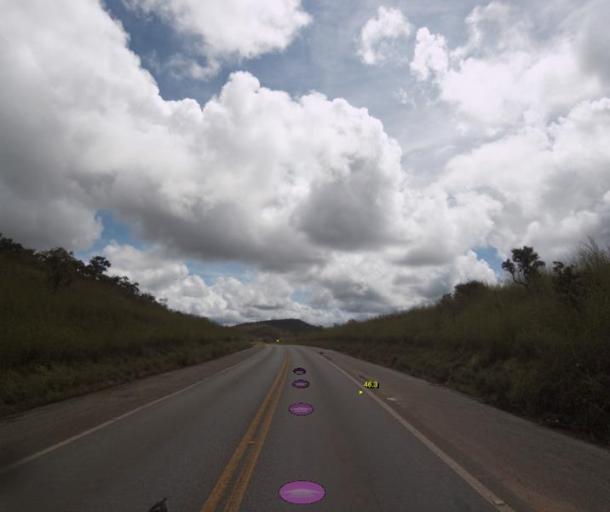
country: BR
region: Goias
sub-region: Pirenopolis
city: Pirenopolis
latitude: -15.7551
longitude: -48.5837
